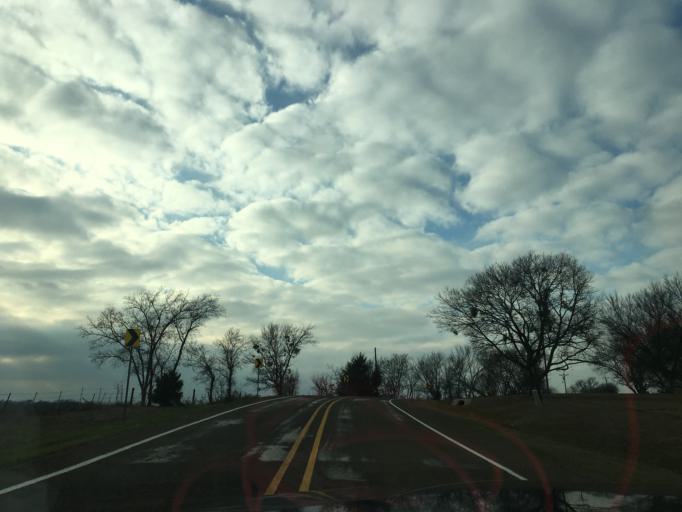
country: US
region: Texas
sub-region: Ellis County
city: Palmer
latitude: 32.4522
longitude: -96.7339
